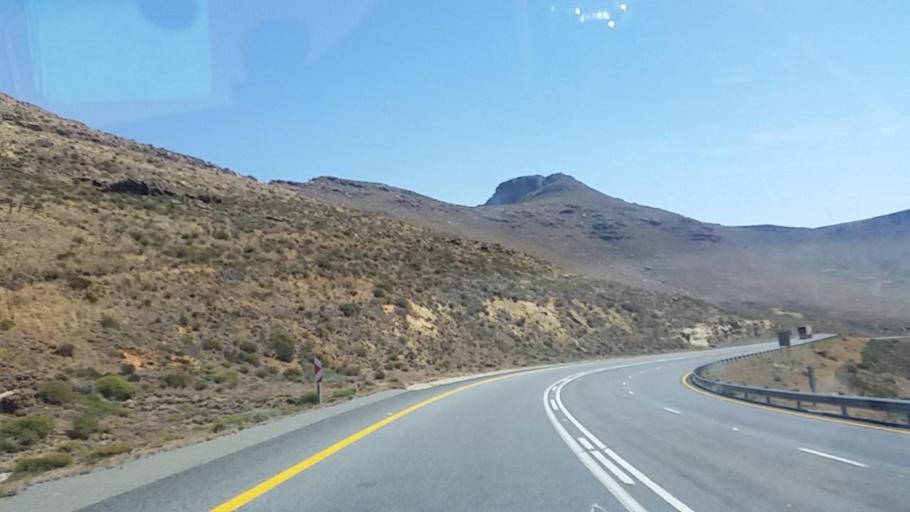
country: ZA
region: Eastern Cape
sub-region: Chris Hani District Municipality
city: Middelburg
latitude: -31.8317
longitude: 24.8564
